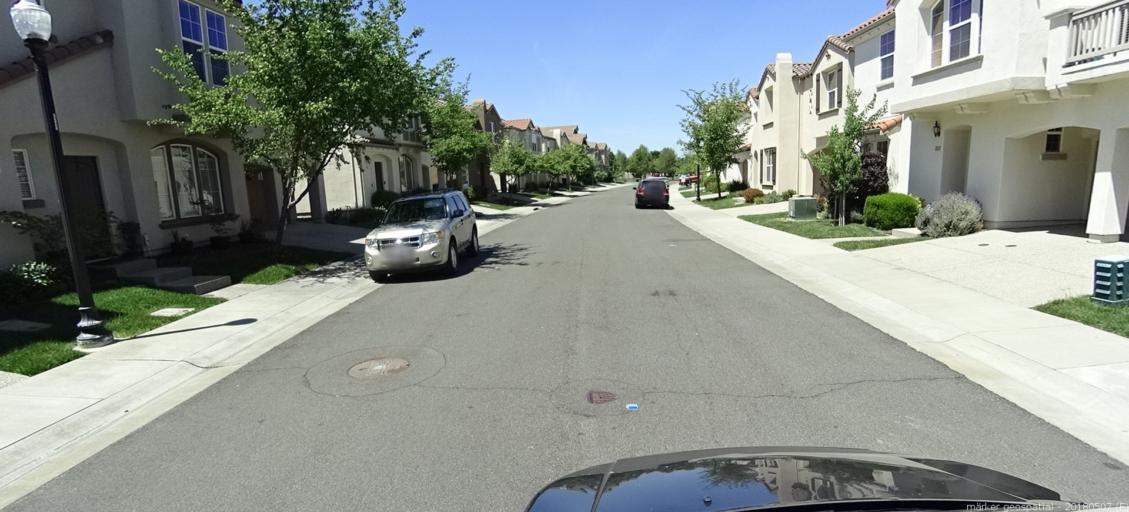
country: US
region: California
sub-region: Sacramento County
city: Elverta
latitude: 38.6704
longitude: -121.5134
